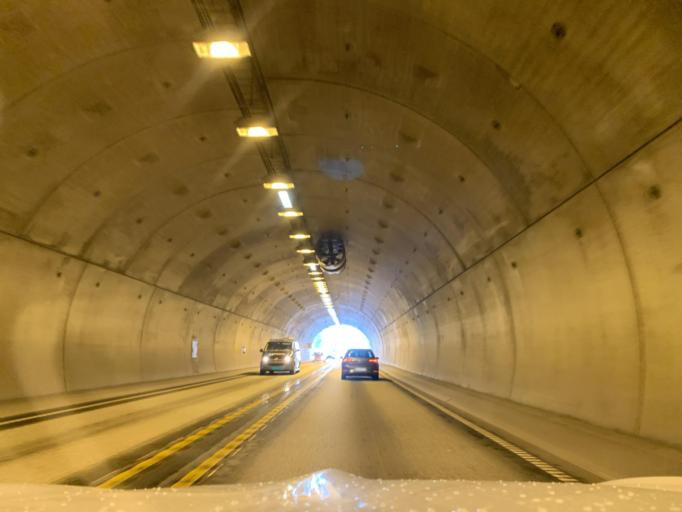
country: NO
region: Rogaland
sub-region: Klepp
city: Kleppe
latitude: 58.7749
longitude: 5.6194
